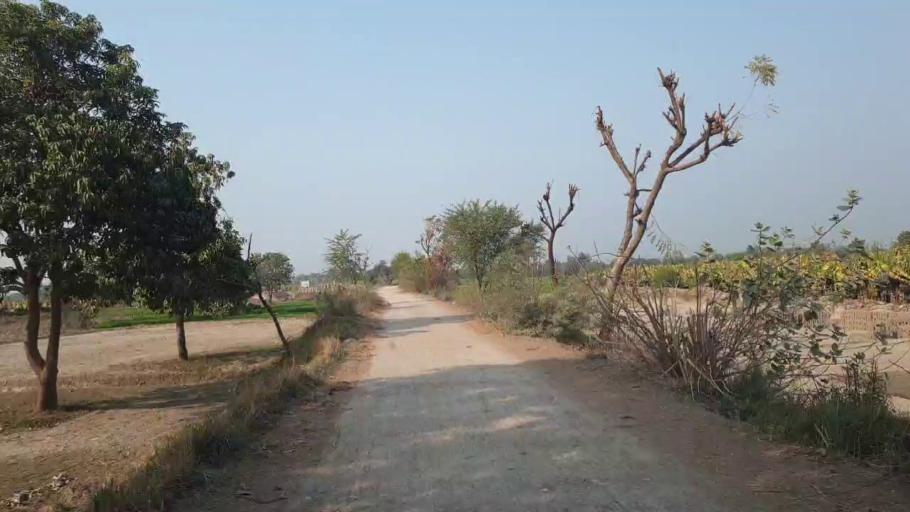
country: PK
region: Sindh
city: Bhit Shah
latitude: 25.8870
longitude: 68.4757
